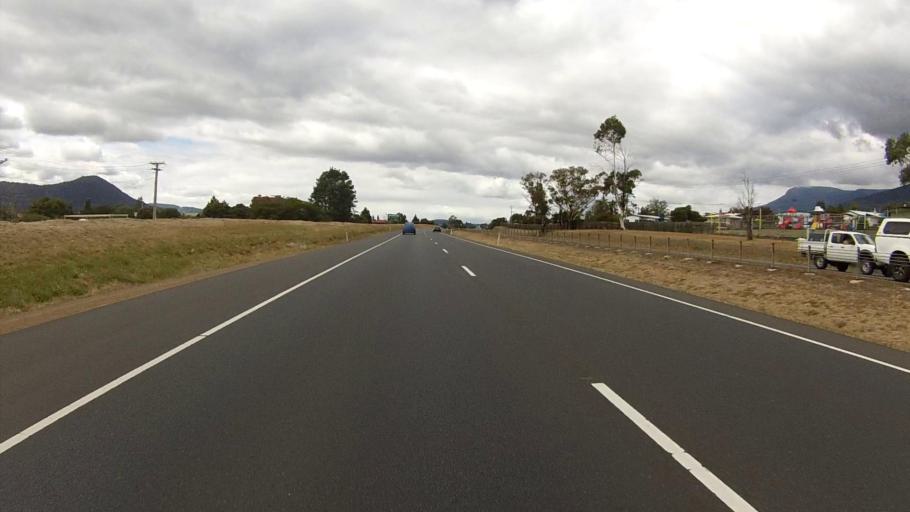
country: AU
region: Tasmania
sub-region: Glenorchy
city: Claremont
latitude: -42.7839
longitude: 147.2408
